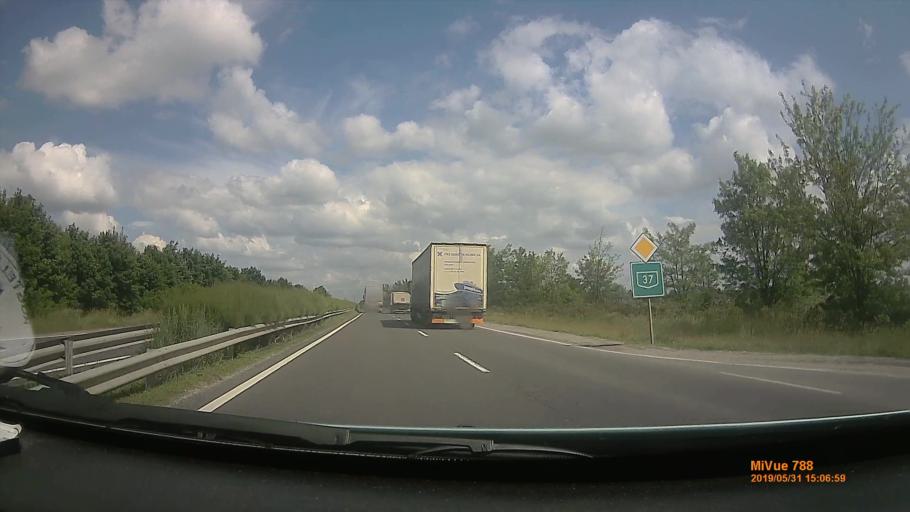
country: HU
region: Borsod-Abauj-Zemplen
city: Onga
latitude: 48.1053
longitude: 20.9073
